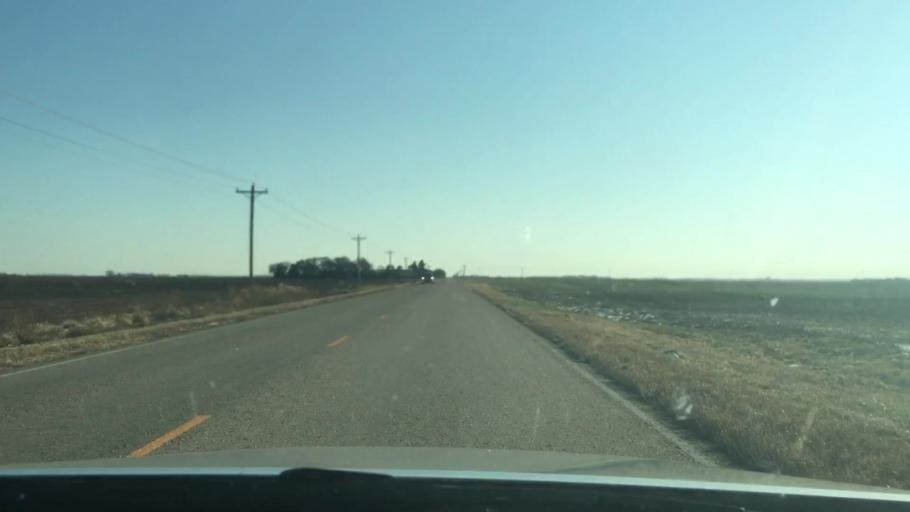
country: US
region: Kansas
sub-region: Reno County
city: Nickerson
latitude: 38.2083
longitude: -98.0877
